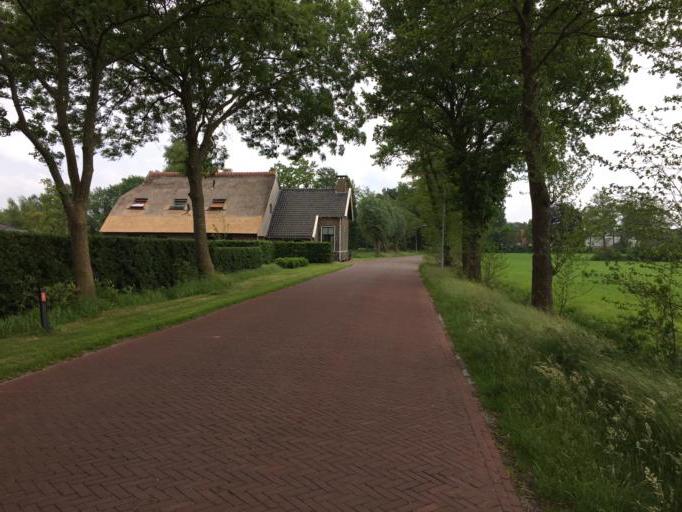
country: NL
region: Drenthe
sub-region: Gemeente Tynaarlo
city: Vries
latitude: 53.1226
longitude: 6.5316
